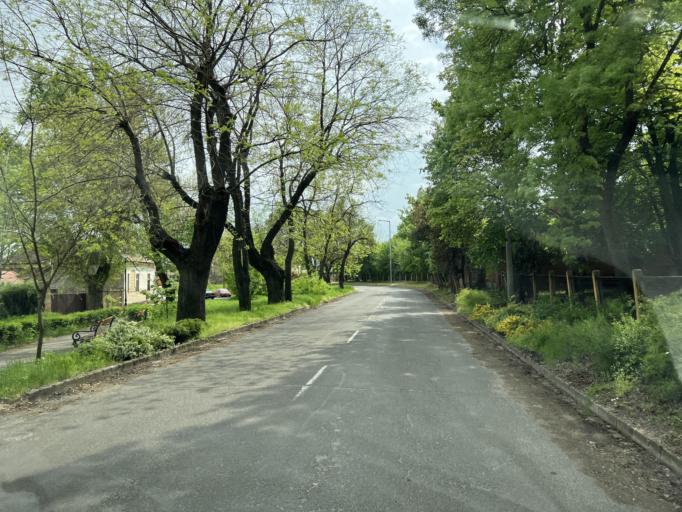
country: HU
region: Pest
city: Nagykoros
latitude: 47.0378
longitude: 19.7606
